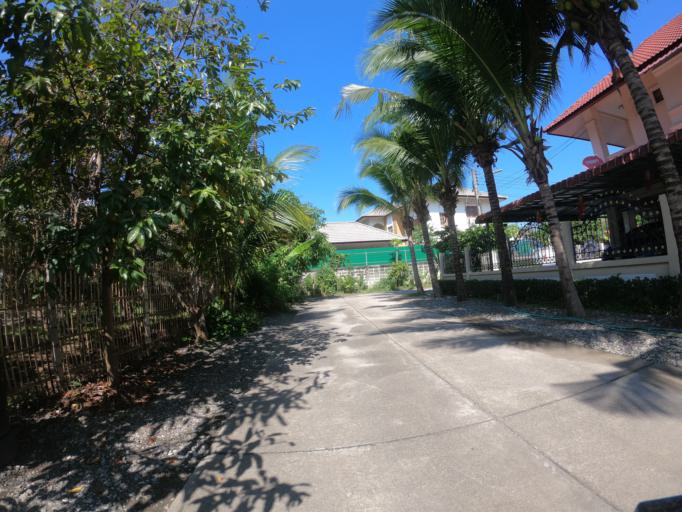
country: TH
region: Chiang Mai
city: Chiang Mai
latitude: 18.7508
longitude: 98.9685
